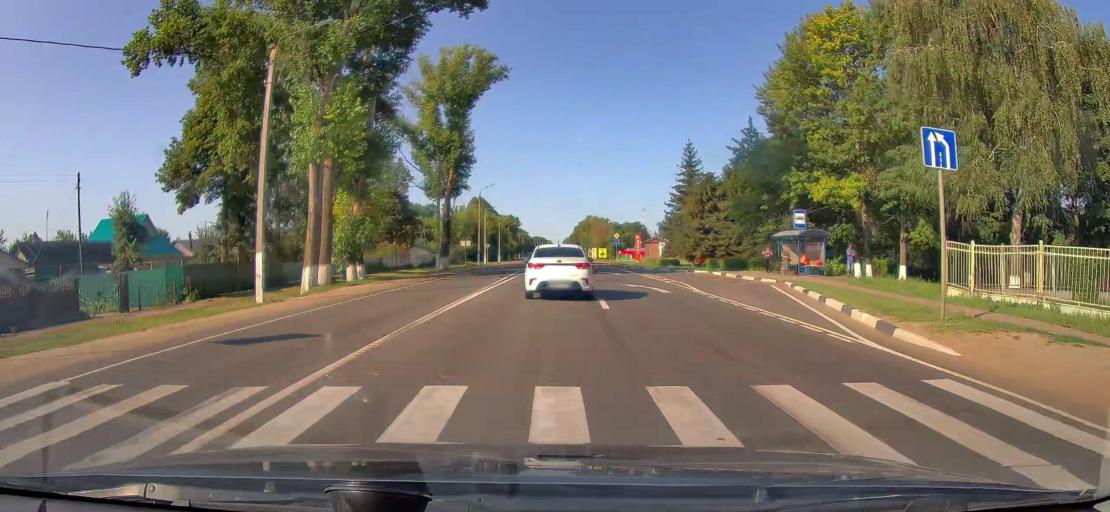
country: RU
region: Orjol
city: Mtsensk
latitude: 53.1815
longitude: 36.4097
